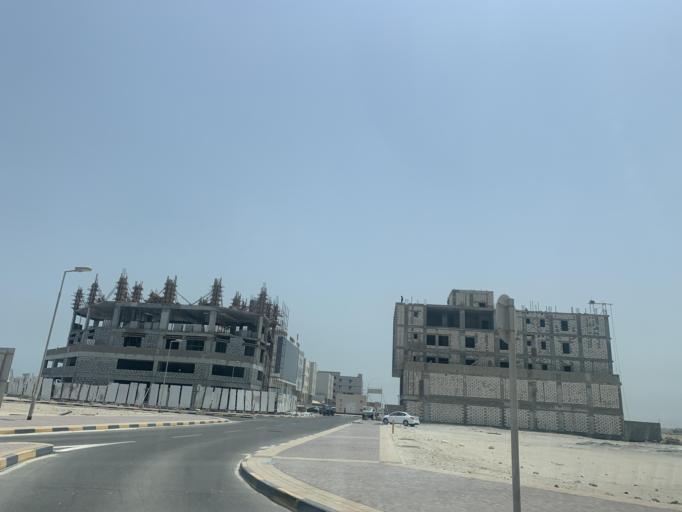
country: BH
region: Muharraq
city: Al Hadd
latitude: 26.2572
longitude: 50.6653
